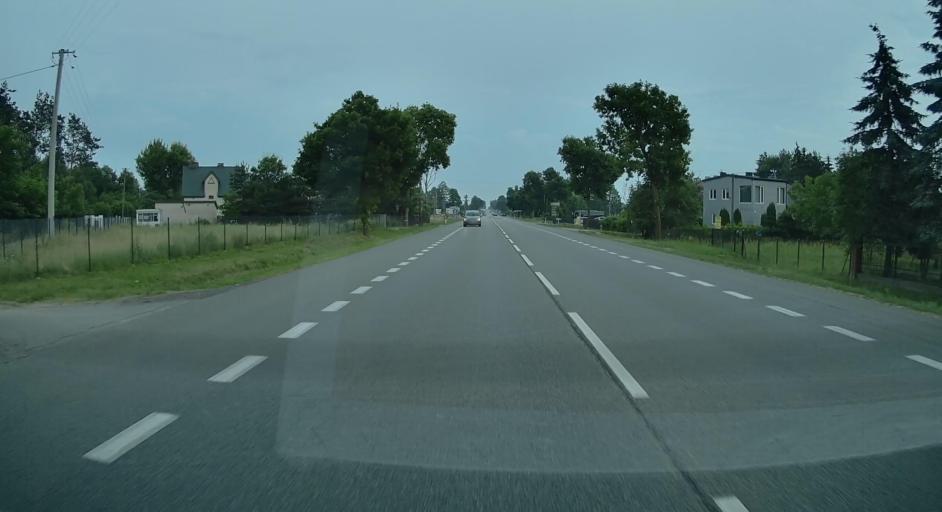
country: PL
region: Masovian Voivodeship
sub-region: Siedlce
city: Siedlce
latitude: 52.1236
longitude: 22.3497
